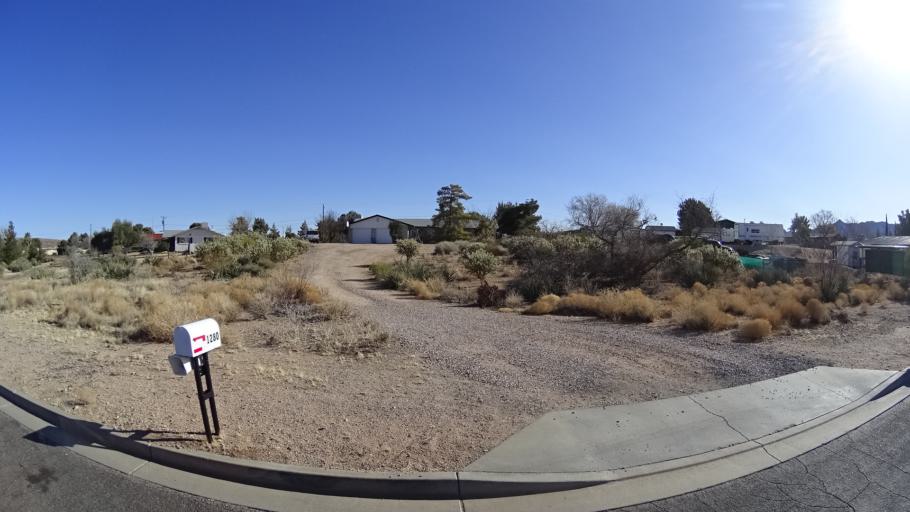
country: US
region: Arizona
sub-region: Mohave County
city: Kingman
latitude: 35.1998
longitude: -114.0049
